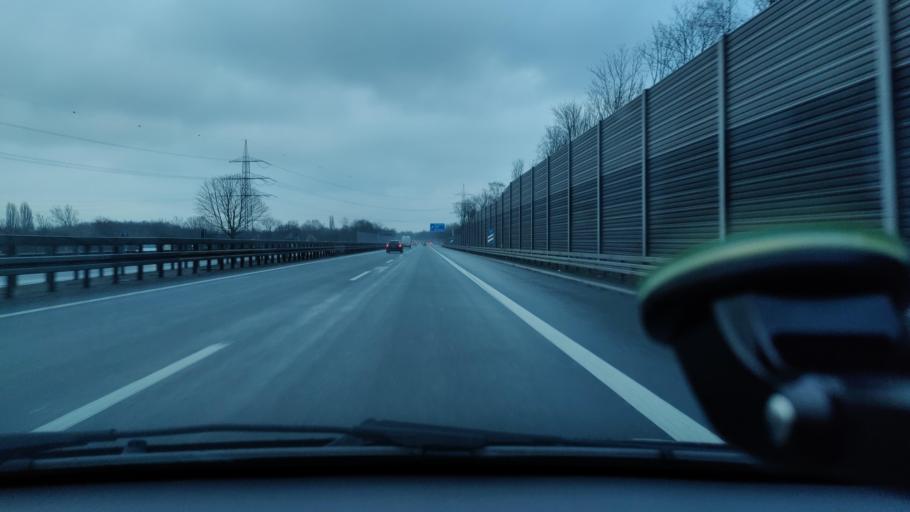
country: DE
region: North Rhine-Westphalia
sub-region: Regierungsbezirk Dusseldorf
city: Essen
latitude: 51.5142
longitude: 7.0384
